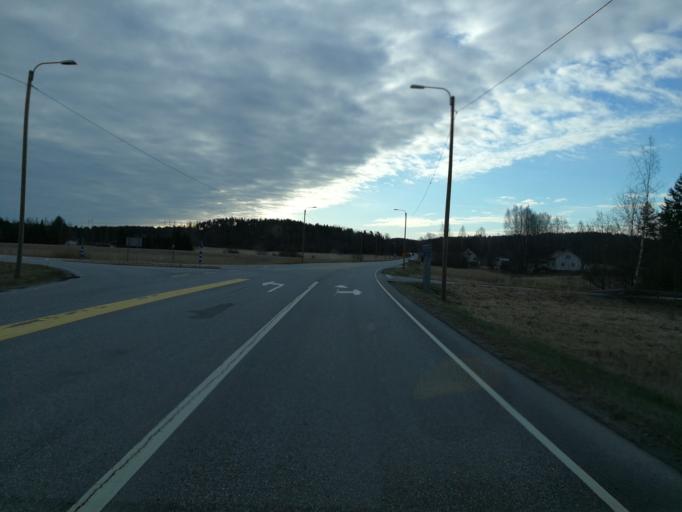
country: FI
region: Varsinais-Suomi
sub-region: Turku
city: Piikkioe
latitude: 60.4348
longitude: 22.5869
